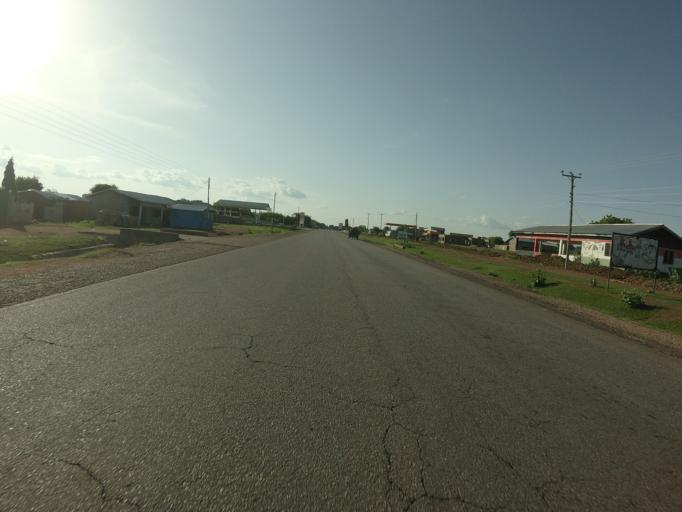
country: GH
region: Upper East
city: Navrongo
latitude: 10.9560
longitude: -1.0972
